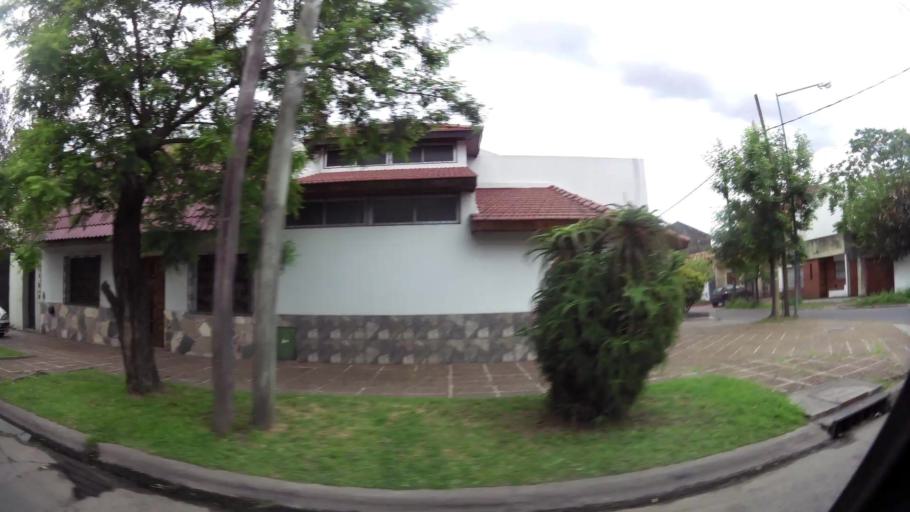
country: AR
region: Buenos Aires
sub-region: Partido de Lanus
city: Lanus
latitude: -34.6915
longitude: -58.3962
